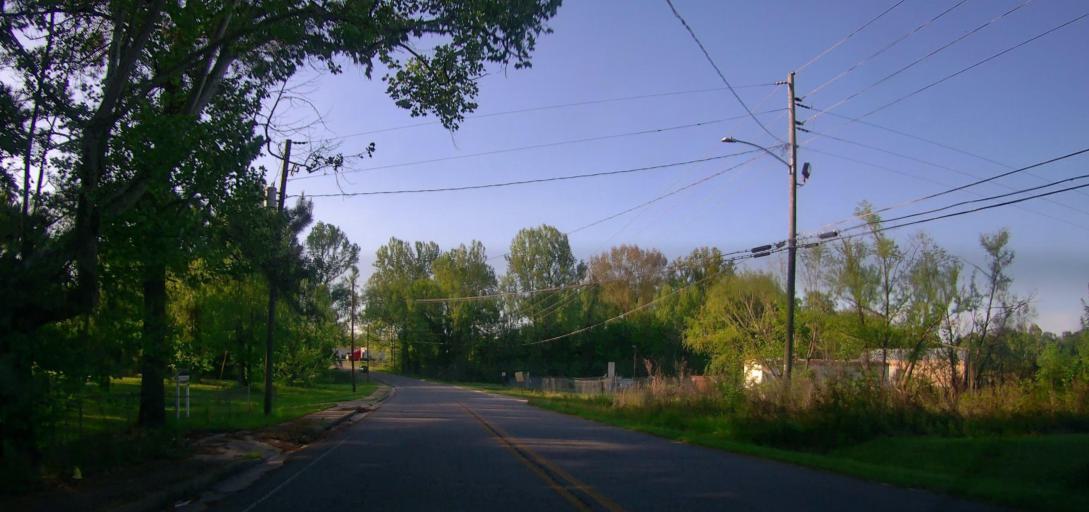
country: US
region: Georgia
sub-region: Macon County
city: Oglethorpe
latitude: 32.2910
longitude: -84.0583
